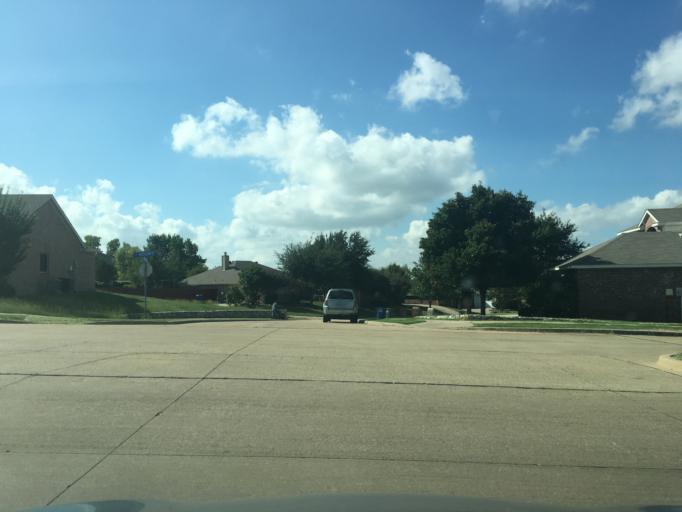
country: US
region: Texas
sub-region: Dallas County
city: Sachse
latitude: 32.9581
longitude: -96.5869
